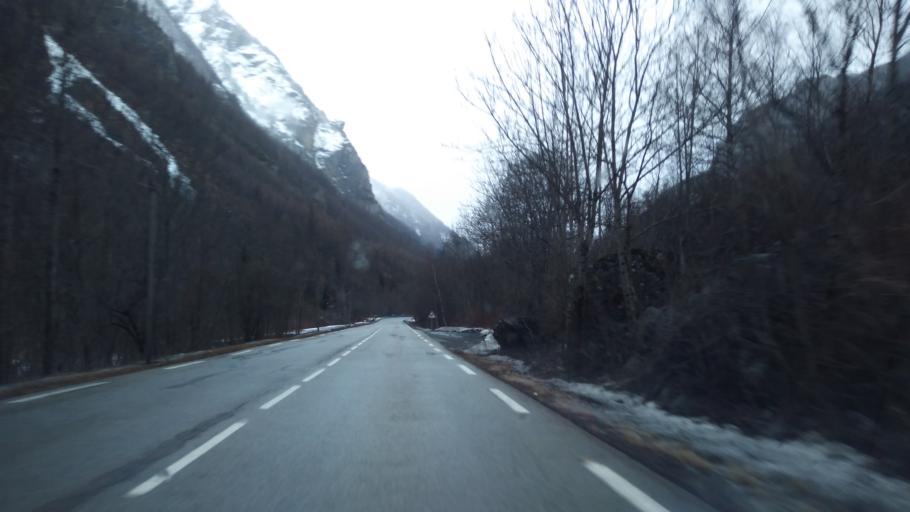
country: FR
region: Rhone-Alpes
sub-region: Departement de l'Isere
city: Mont-de-Lans
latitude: 45.0377
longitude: 6.1990
